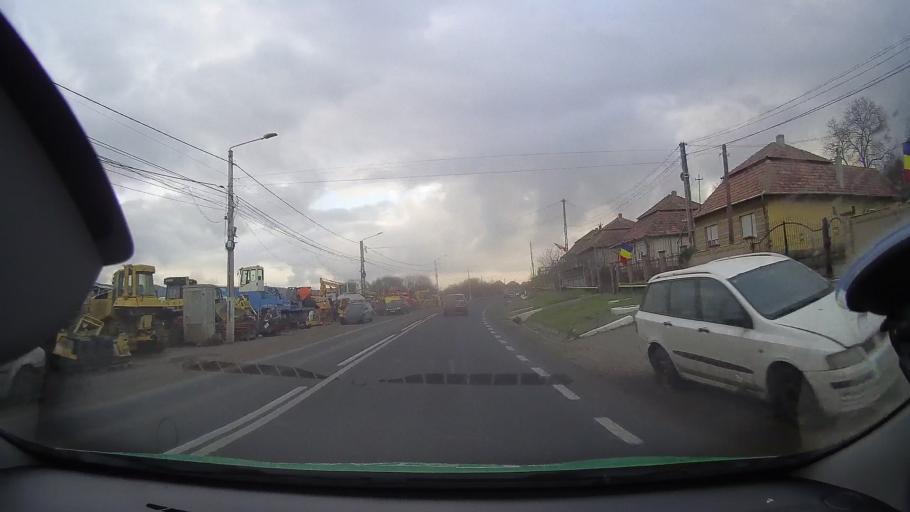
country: RO
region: Cluj
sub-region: Comuna Viisoara
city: Viisoara
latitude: 46.5114
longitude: 23.9183
